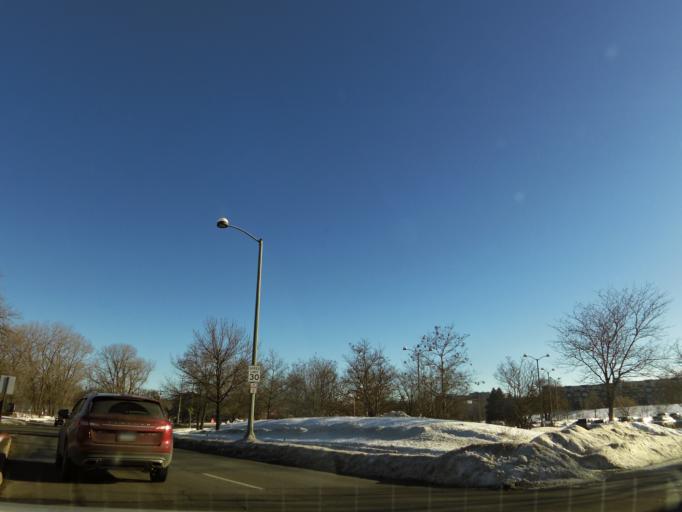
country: US
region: Minnesota
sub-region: Hennepin County
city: Saint Louis Park
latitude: 44.9378
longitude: -93.3419
